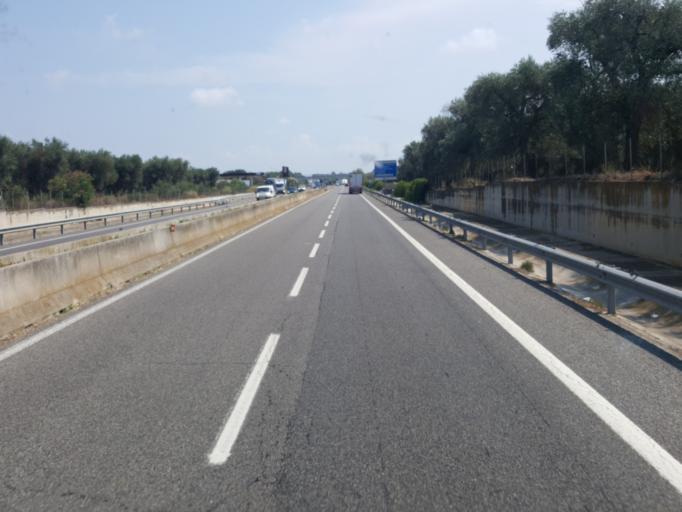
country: IT
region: Apulia
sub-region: Provincia di Brindisi
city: Torchiarolo
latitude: 40.4929
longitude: 18.0369
